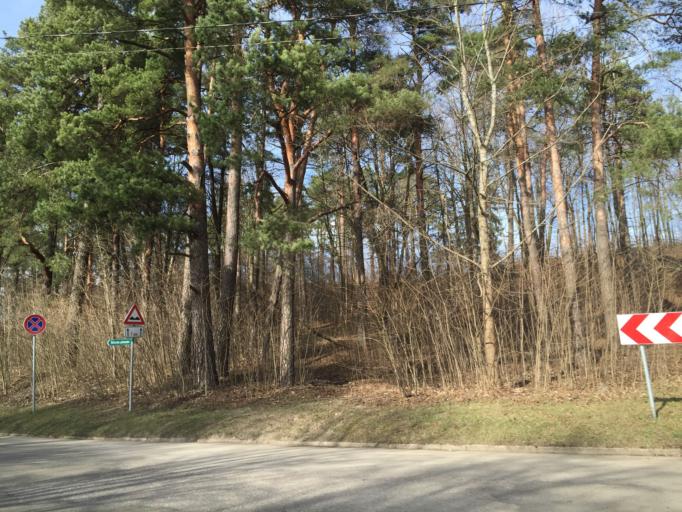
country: LV
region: Ogre
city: Ogre
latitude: 56.8125
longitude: 24.6136
